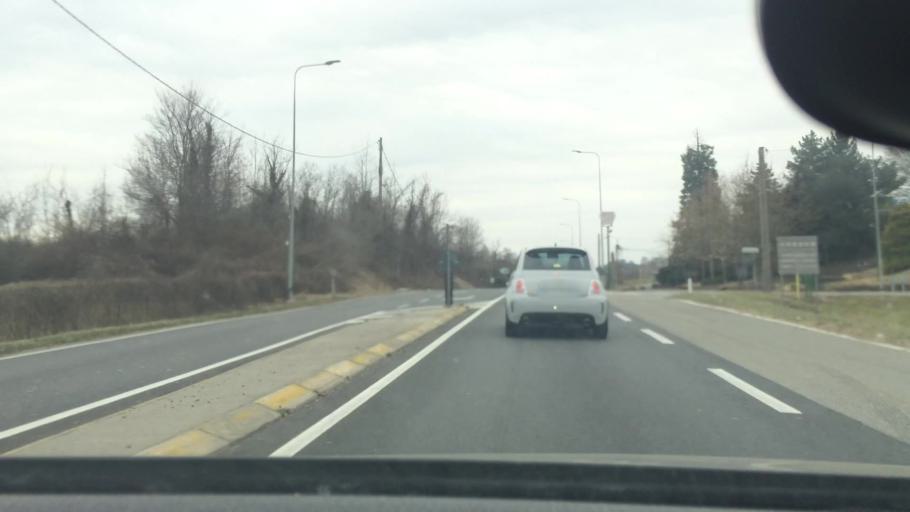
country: IT
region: Lombardy
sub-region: Provincia di Como
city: Nobile-Monguzzo
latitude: 45.7729
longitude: 9.2301
